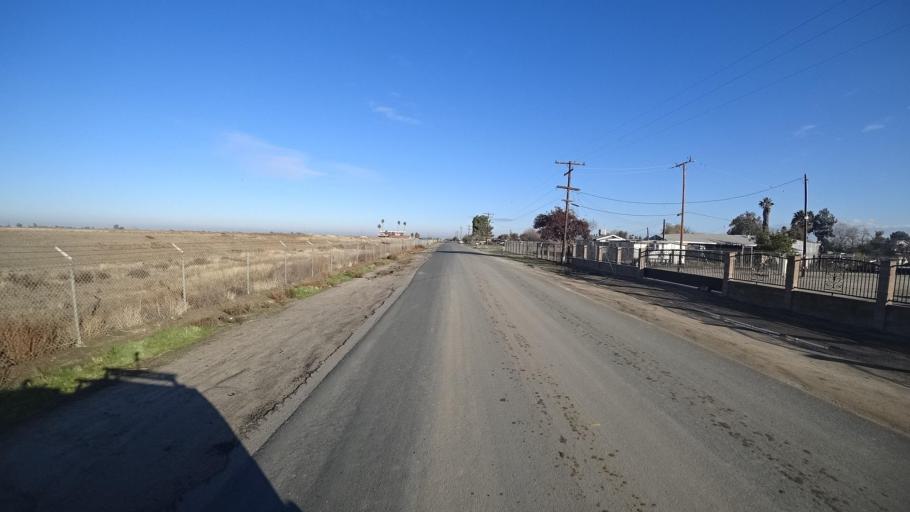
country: US
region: California
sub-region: Kern County
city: Delano
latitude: 35.7717
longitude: -119.2852
